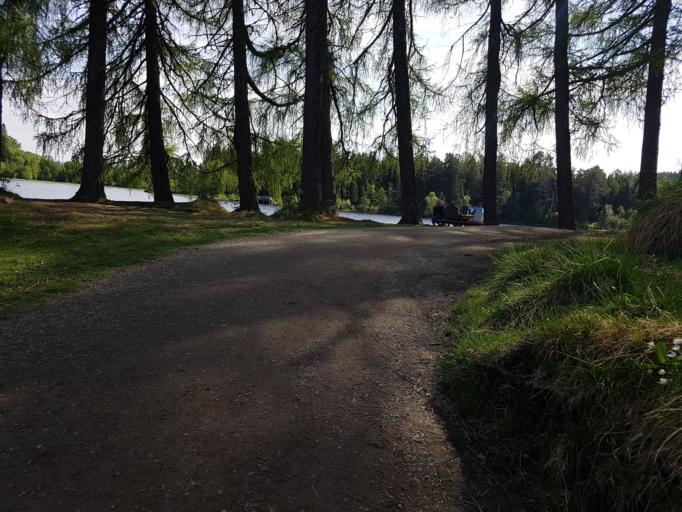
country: NO
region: Sor-Trondelag
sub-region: Trondheim
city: Trondheim
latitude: 63.4220
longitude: 10.3428
